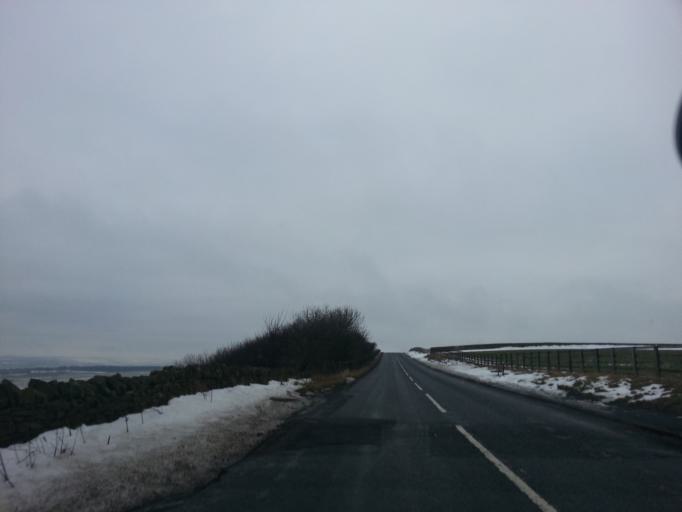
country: GB
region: England
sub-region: County Durham
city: Crook
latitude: 54.7367
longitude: -1.7571
